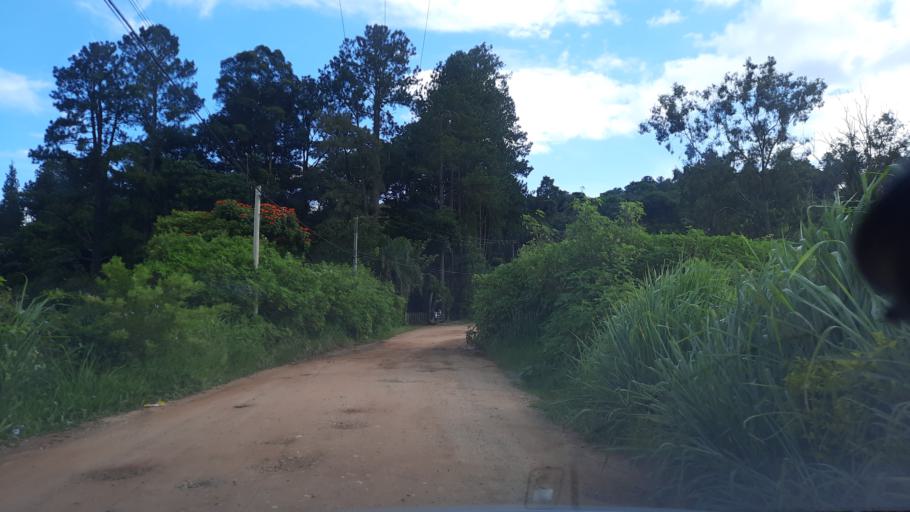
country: BR
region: Sao Paulo
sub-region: Atibaia
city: Atibaia
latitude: -23.0806
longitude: -46.5093
